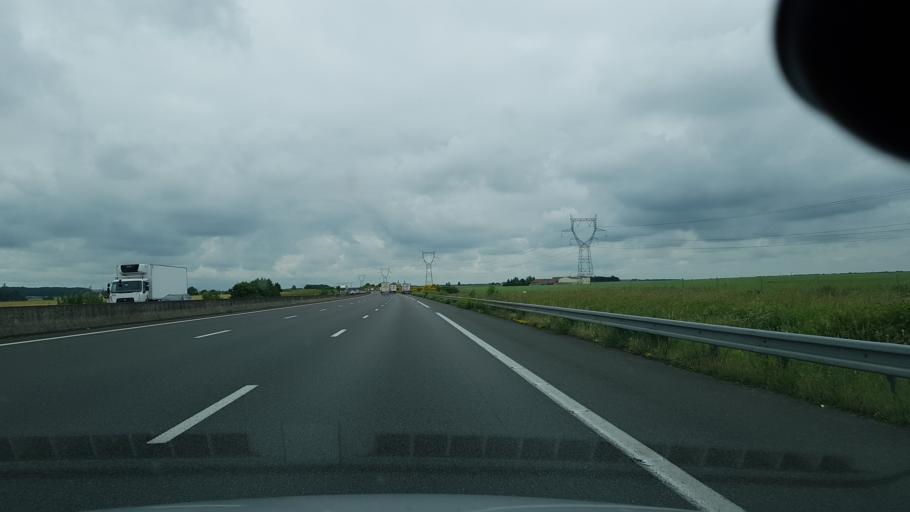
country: FR
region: Centre
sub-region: Departement du Loir-et-Cher
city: Herbault
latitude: 47.6170
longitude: 1.1774
